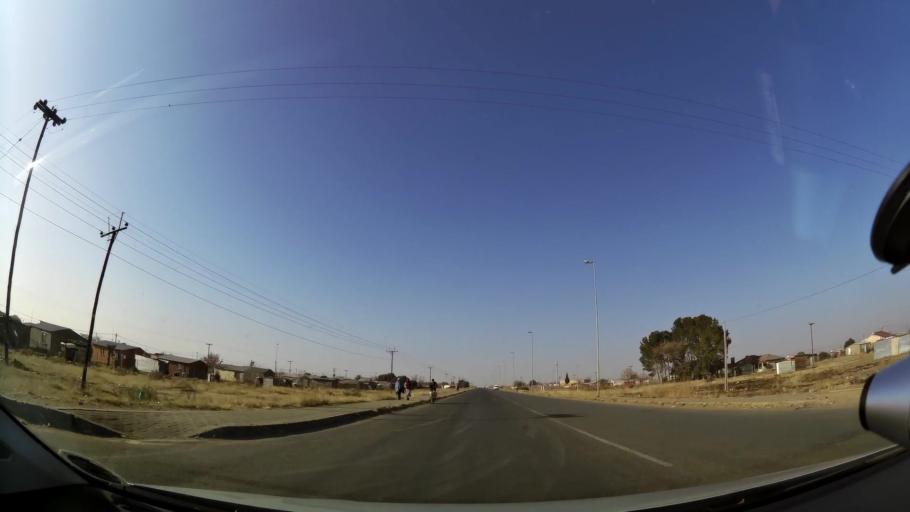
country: ZA
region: Orange Free State
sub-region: Mangaung Metropolitan Municipality
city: Bloemfontein
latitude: -29.1767
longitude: 26.2648
